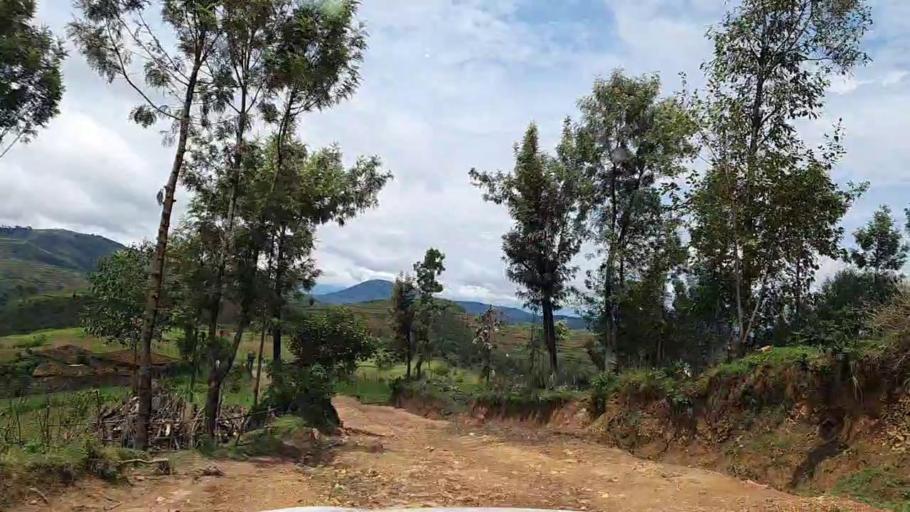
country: RW
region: Southern Province
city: Gikongoro
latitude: -2.3394
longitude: 29.5129
